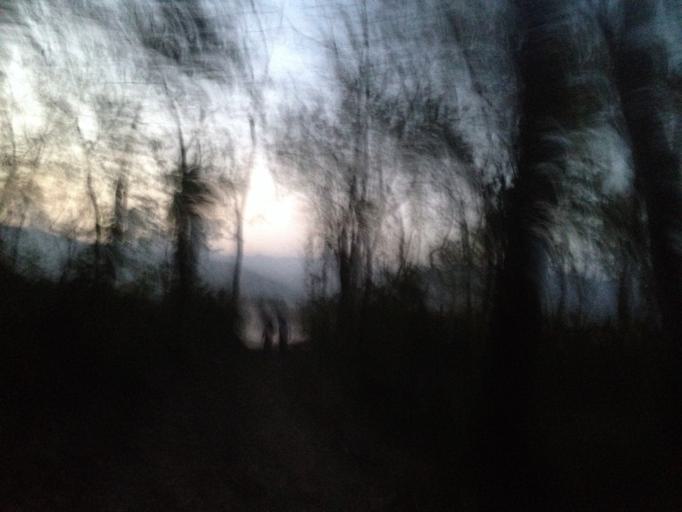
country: NP
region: Central Region
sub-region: Narayani Zone
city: Bharatpur
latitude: 27.6946
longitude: 84.4093
